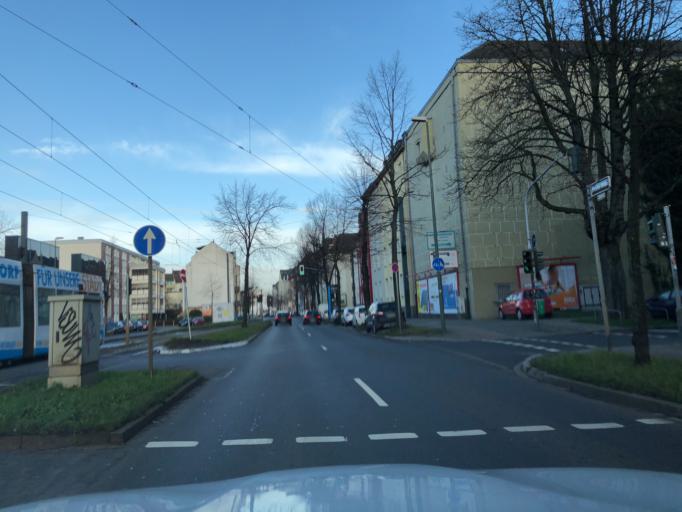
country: DE
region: North Rhine-Westphalia
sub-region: Regierungsbezirk Dusseldorf
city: Dusseldorf
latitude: 51.2145
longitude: 6.8222
